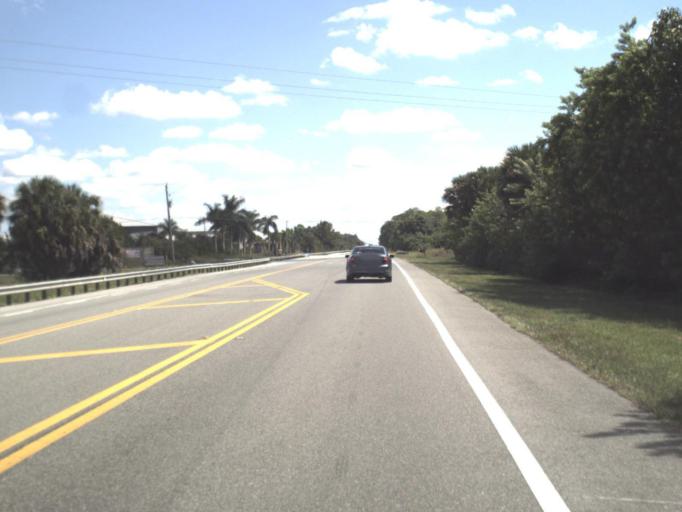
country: US
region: Florida
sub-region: Collier County
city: Lely Resort
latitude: 26.0266
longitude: -81.6418
